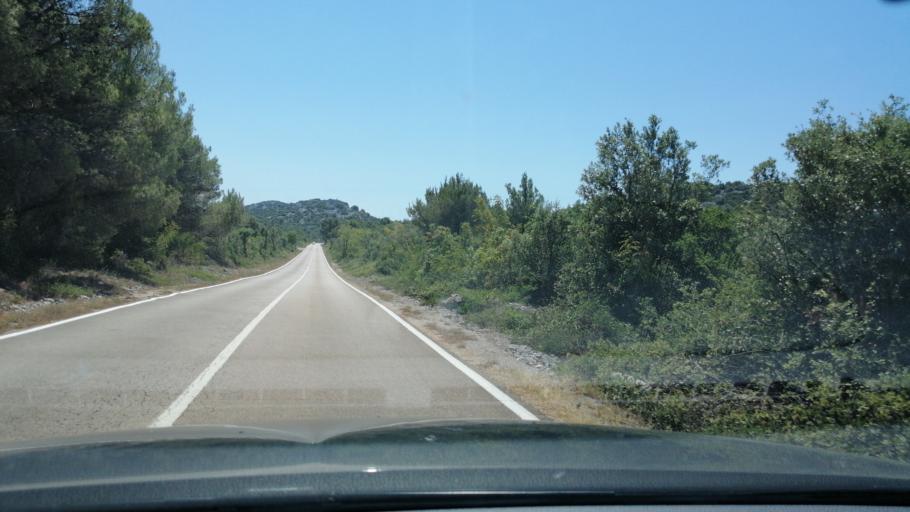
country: HR
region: Sibensko-Kniniska
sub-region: Grad Sibenik
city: Pirovac
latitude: 43.8441
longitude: 15.6870
